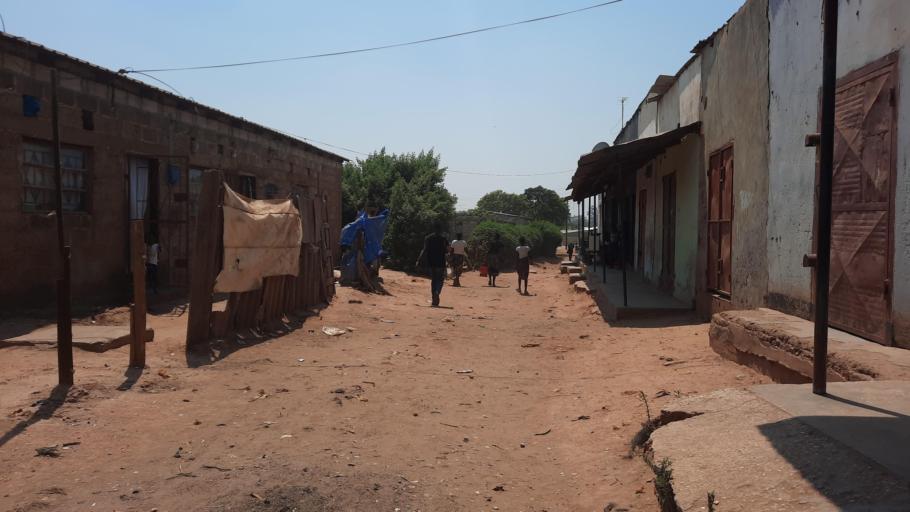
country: ZM
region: Lusaka
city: Lusaka
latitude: -15.3982
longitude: 28.3740
